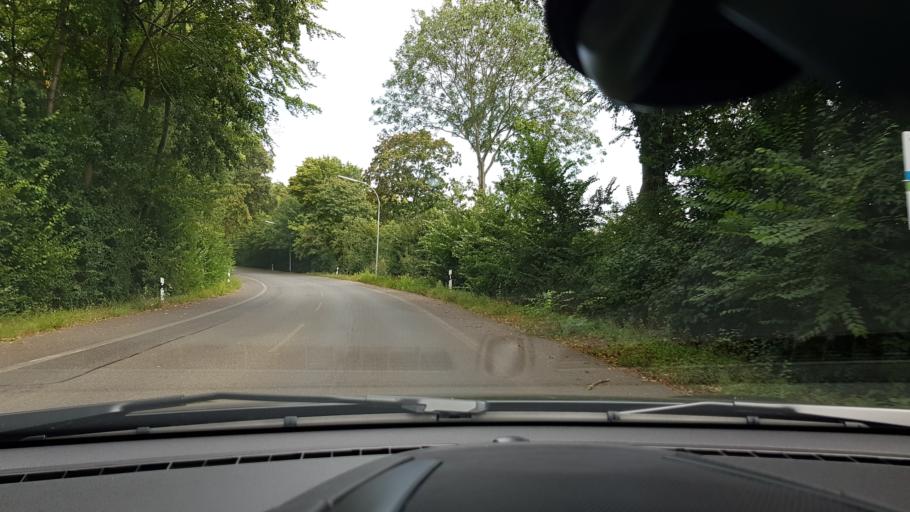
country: DE
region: North Rhine-Westphalia
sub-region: Regierungsbezirk Dusseldorf
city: Grevenbroich
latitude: 51.0479
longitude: 6.5787
